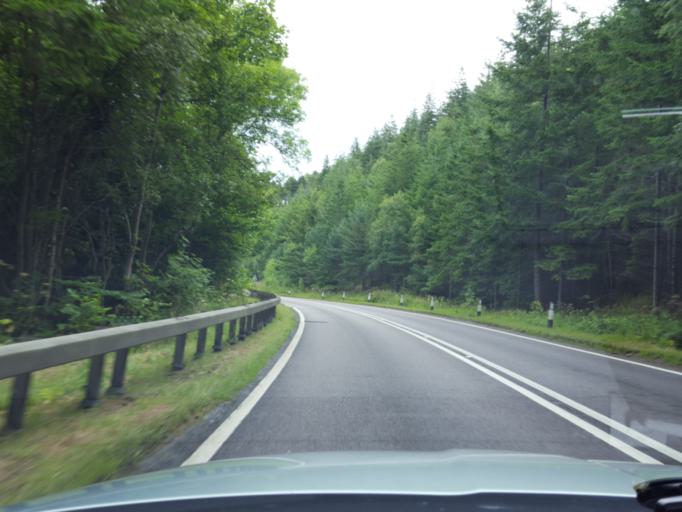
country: GB
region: Scotland
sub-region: Moray
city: Rothes
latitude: 57.4811
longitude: -3.1972
